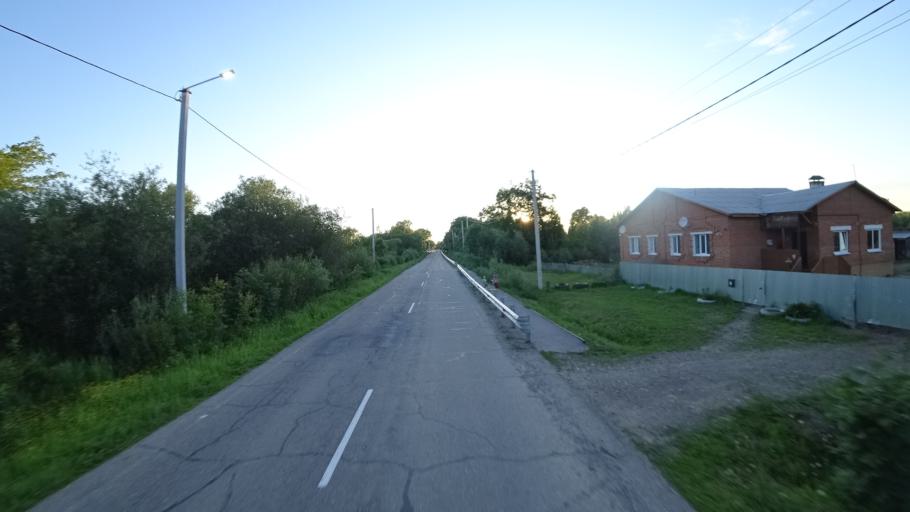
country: RU
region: Khabarovsk Krai
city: Khor
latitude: 47.8533
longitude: 134.9758
